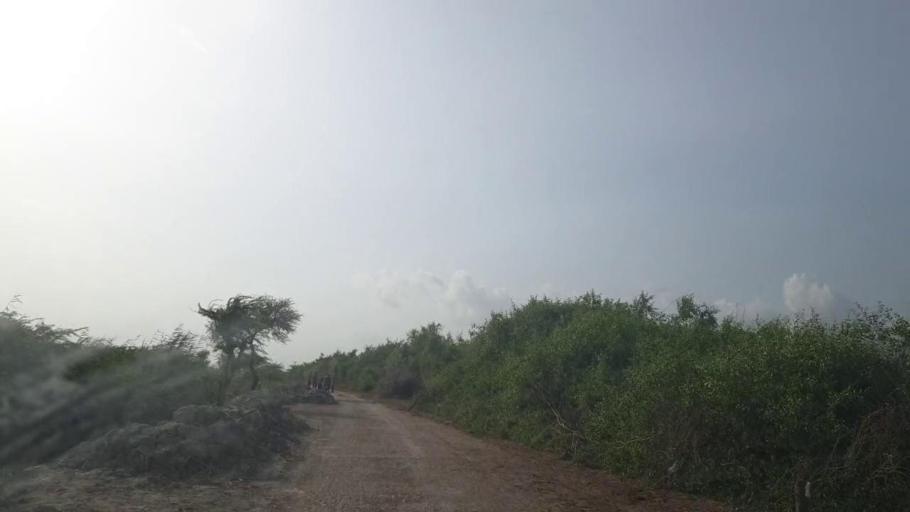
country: PK
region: Sindh
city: Tando Bago
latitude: 24.7611
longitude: 69.0809
